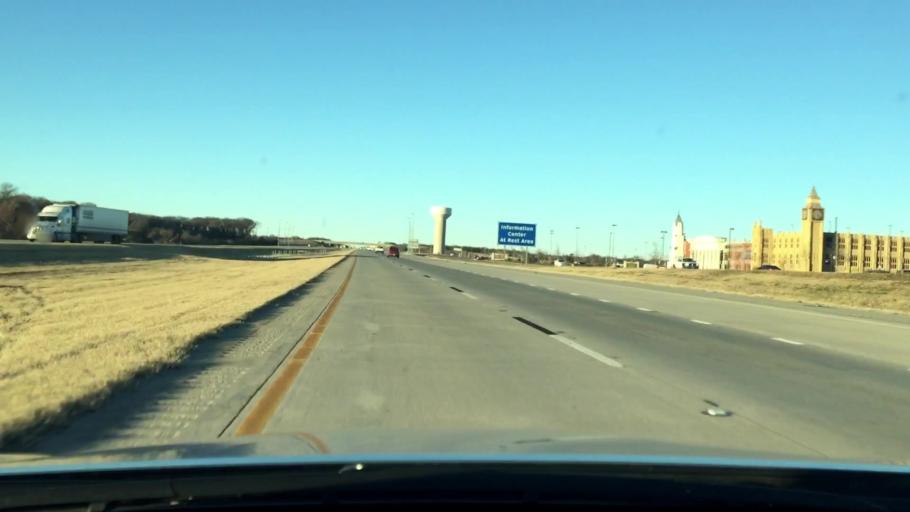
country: US
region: Texas
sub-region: Cooke County
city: Gainesville
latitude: 33.7564
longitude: -97.1345
